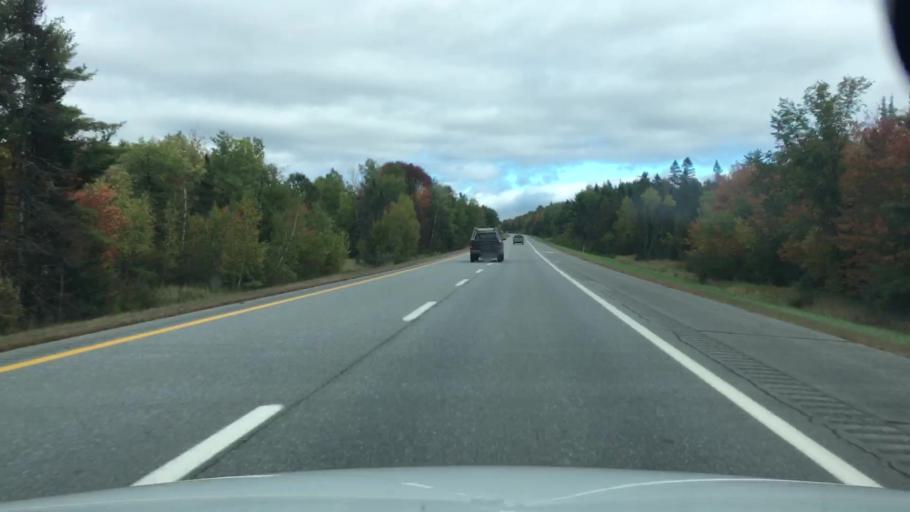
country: US
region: Maine
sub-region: Penobscot County
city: Carmel
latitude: 44.7752
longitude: -69.0419
